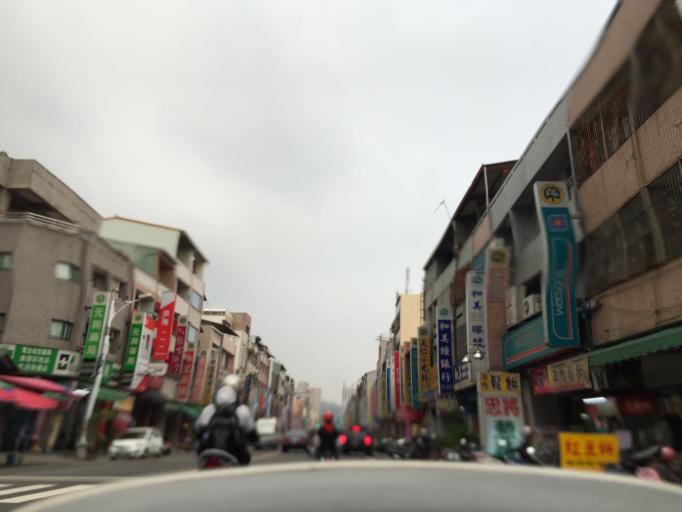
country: TW
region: Taiwan
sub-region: Taichung City
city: Taichung
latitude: 24.0665
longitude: 120.6989
